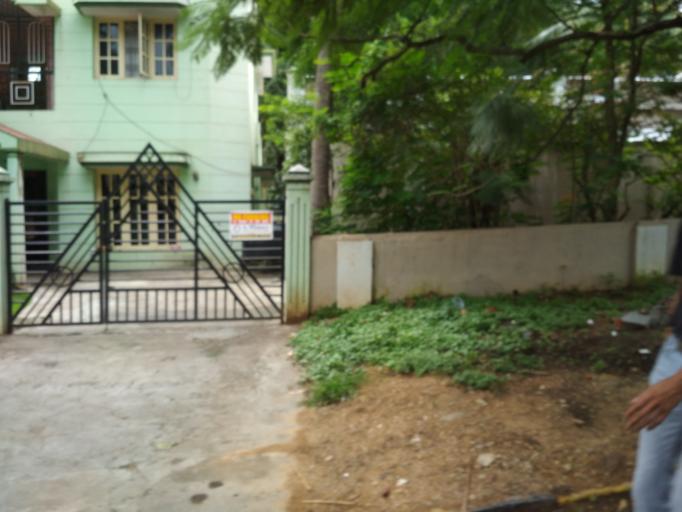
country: IN
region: Karnataka
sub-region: Mysore
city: Mysore
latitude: 12.3273
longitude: 76.6278
